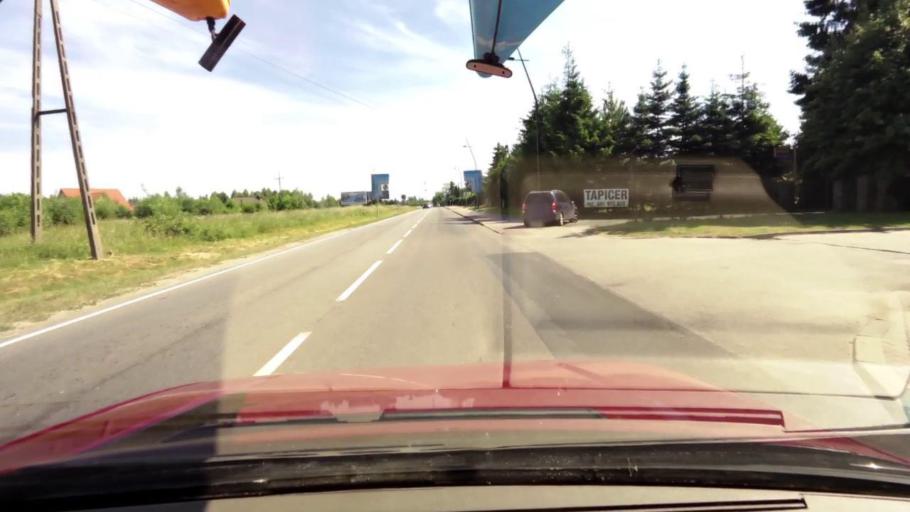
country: PL
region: Pomeranian Voivodeship
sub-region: Powiat slupski
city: Kobylnica
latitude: 54.4372
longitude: 16.9976
